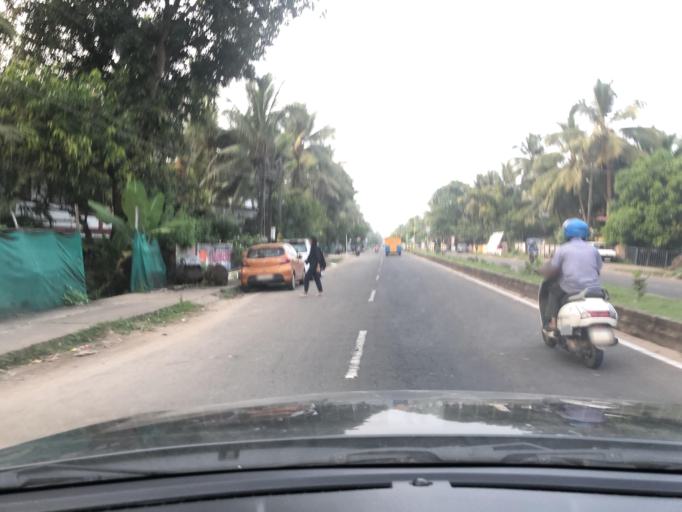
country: IN
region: Kerala
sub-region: Kozhikode
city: Kozhikode
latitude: 11.2944
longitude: 75.7573
